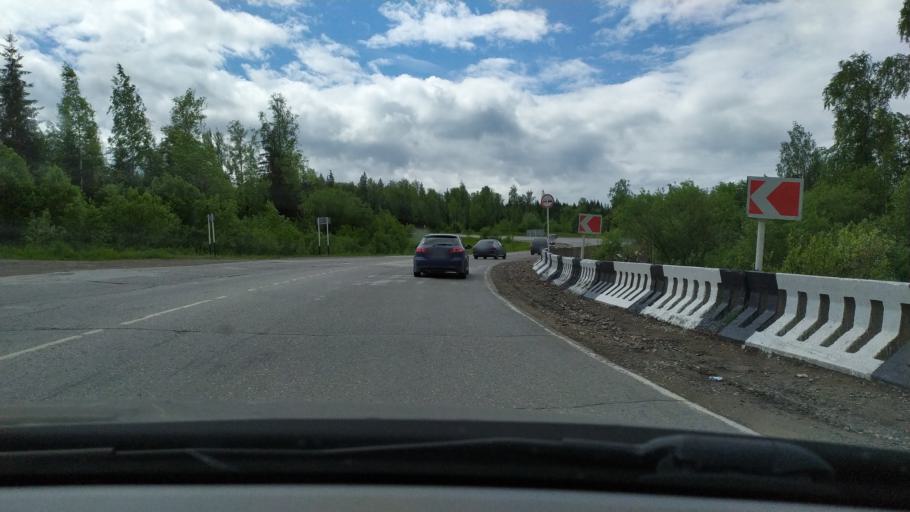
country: RU
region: Perm
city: Gremyachinsk
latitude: 58.4402
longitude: 57.8870
